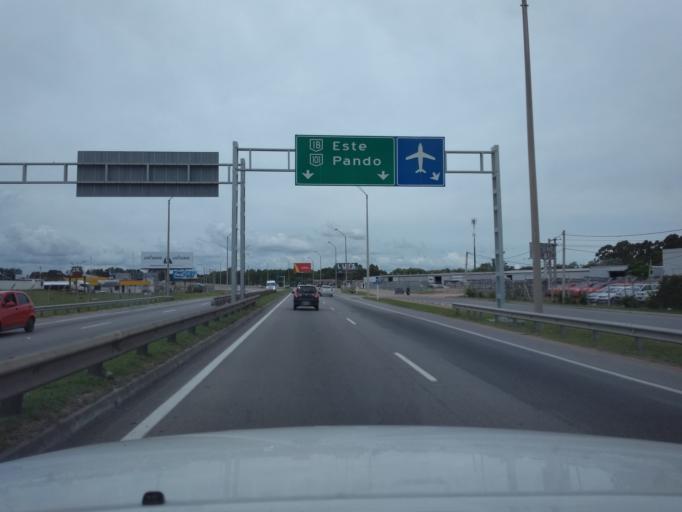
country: UY
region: Canelones
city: Barra de Carrasco
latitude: -34.8441
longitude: -56.0184
